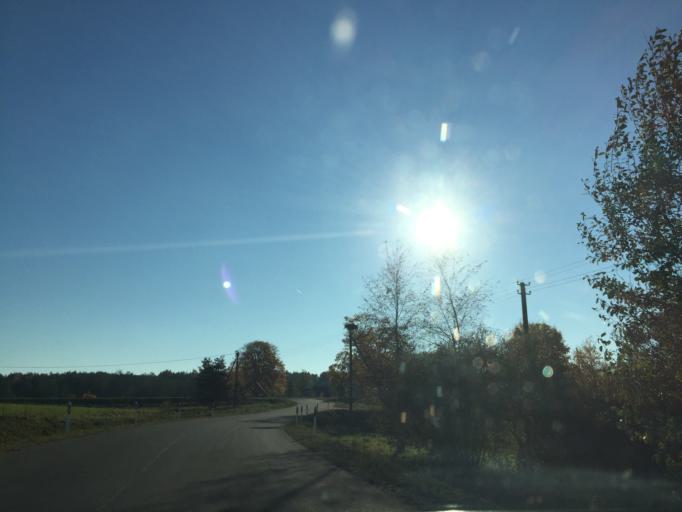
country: LT
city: Plateliai
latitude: 56.0689
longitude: 21.8561
